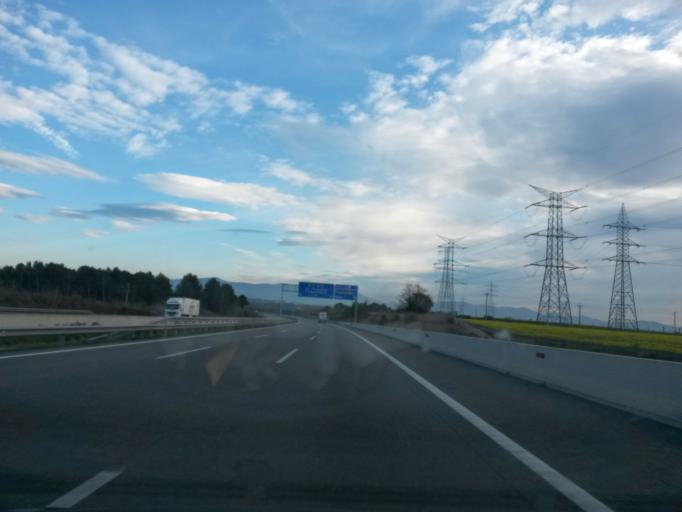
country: ES
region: Catalonia
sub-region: Provincia de Girona
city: Garrigas
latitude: 42.2021
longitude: 2.9358
